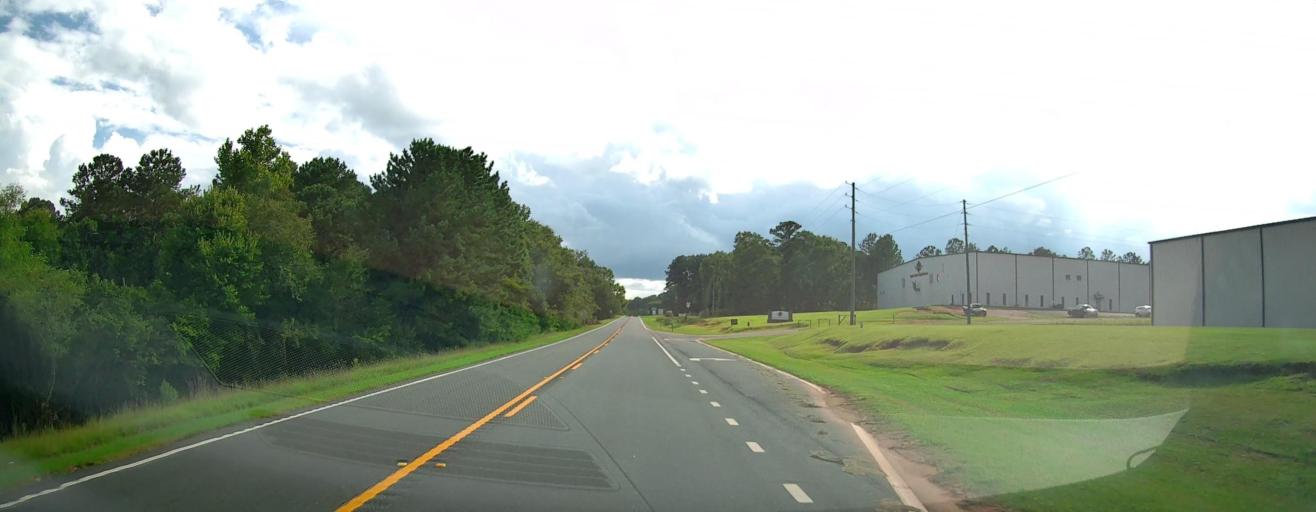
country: US
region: Georgia
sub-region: Meriwether County
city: Manchester
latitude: 32.9931
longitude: -84.5746
